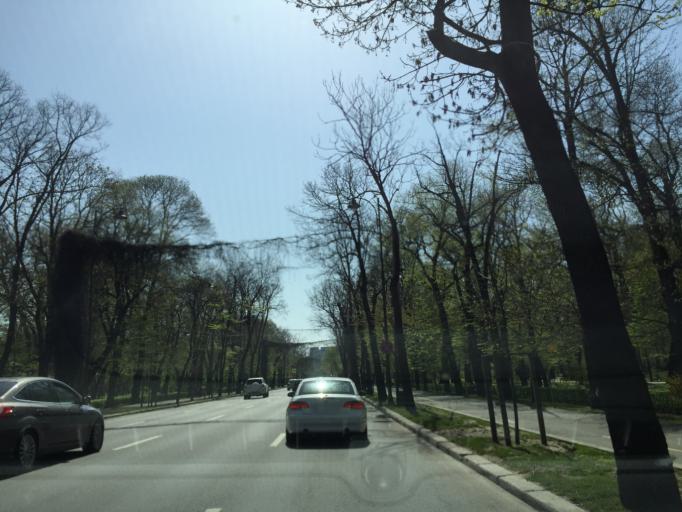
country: RO
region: Bucuresti
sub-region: Municipiul Bucuresti
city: Bucuresti
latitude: 44.4587
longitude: 26.0823
